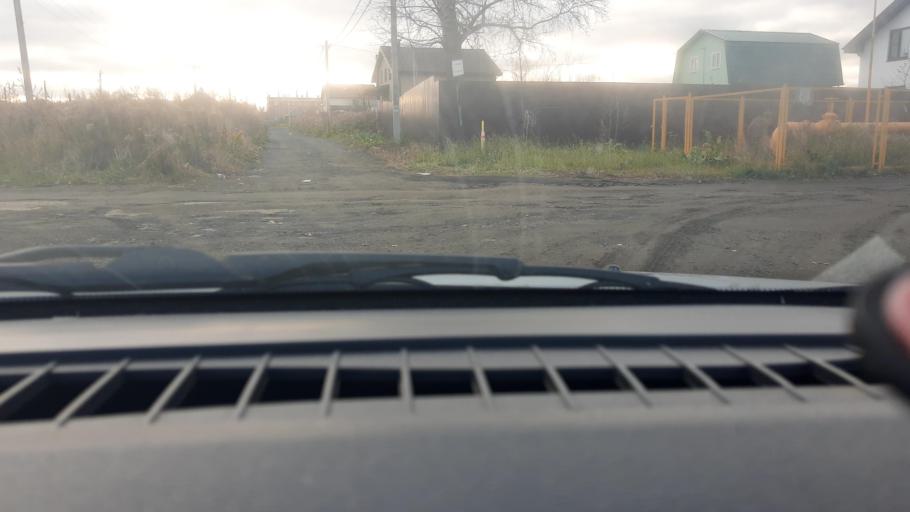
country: RU
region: Nizjnij Novgorod
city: Afonino
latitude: 56.2680
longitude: 44.0513
